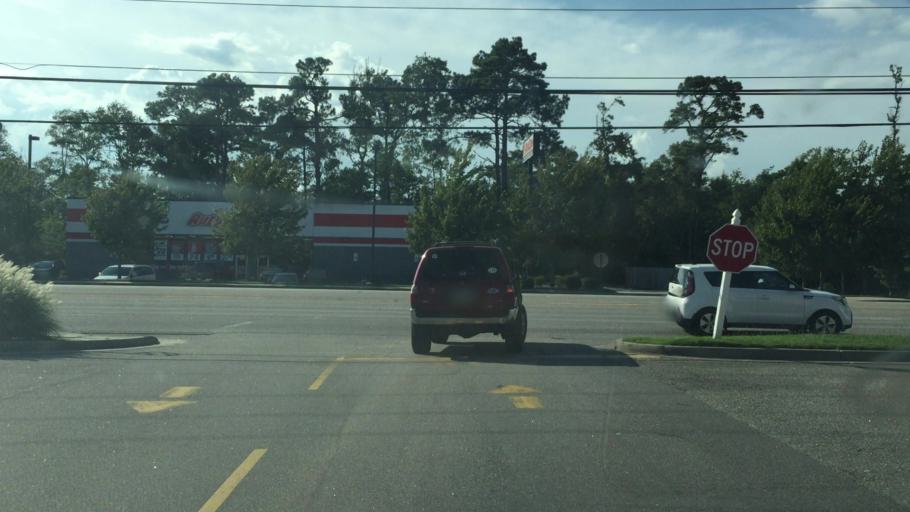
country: US
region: South Carolina
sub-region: Horry County
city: North Myrtle Beach
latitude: 33.8311
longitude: -78.6759
